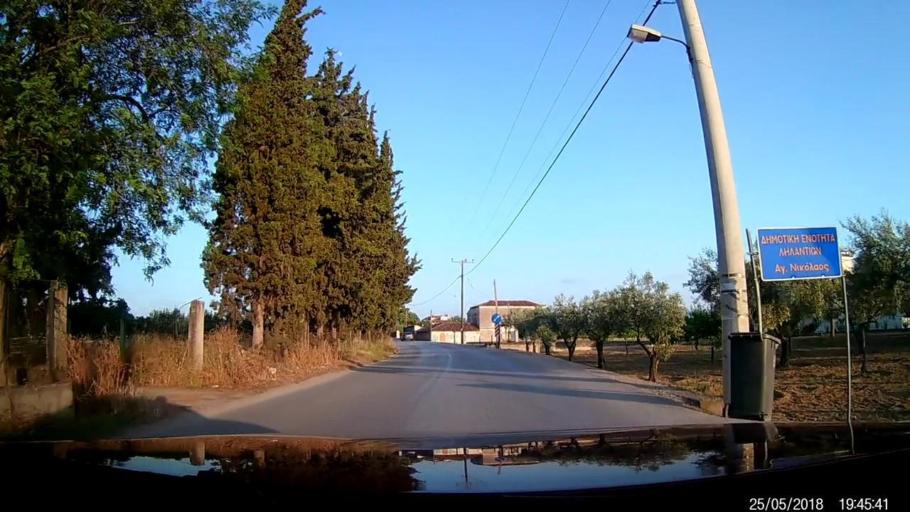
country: GR
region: Central Greece
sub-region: Nomos Evvoias
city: Ayios Nikolaos
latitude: 38.4309
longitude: 23.6348
